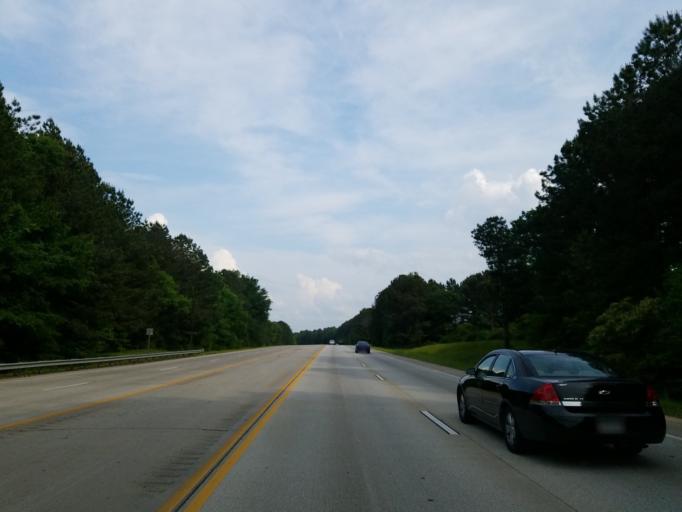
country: US
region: Georgia
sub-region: Cobb County
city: Powder Springs
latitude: 33.8347
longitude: -84.6783
